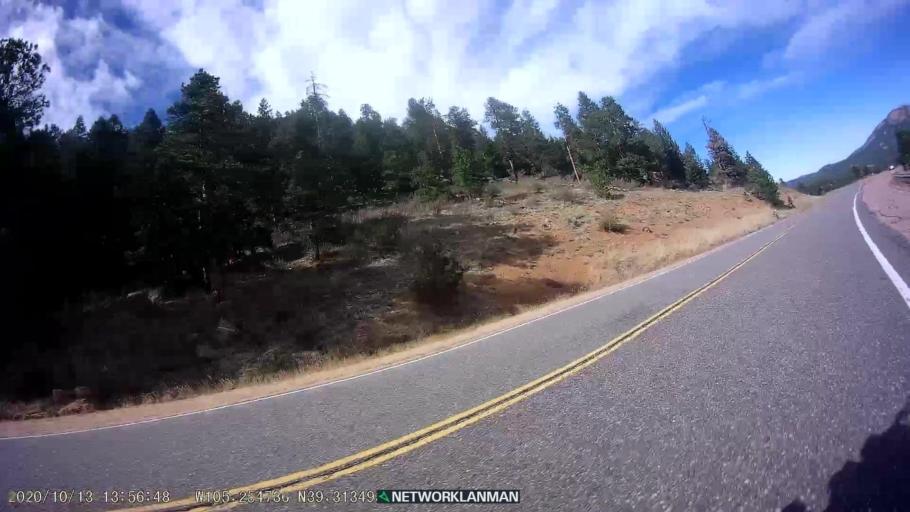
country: US
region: Colorado
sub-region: Douglas County
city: Roxborough Park
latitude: 39.3137
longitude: -105.2546
